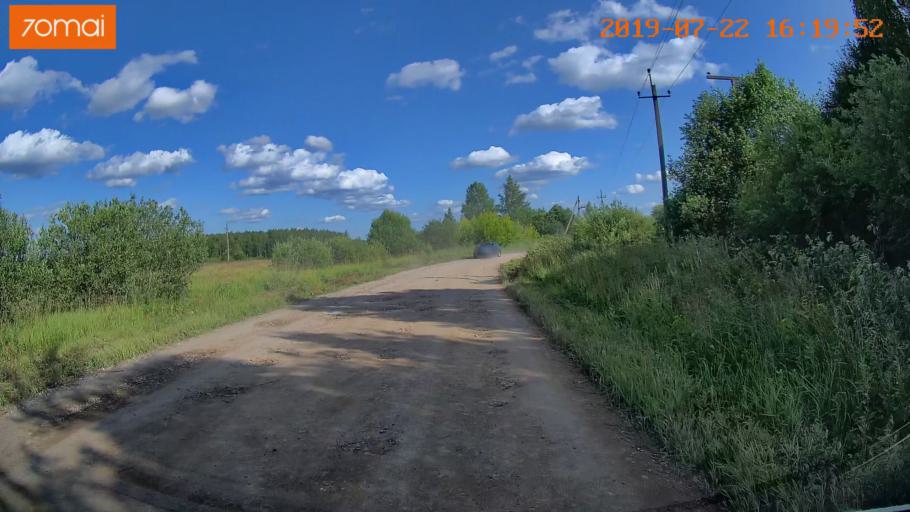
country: RU
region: Ivanovo
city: Novo-Talitsy
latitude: 57.0656
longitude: 40.8930
